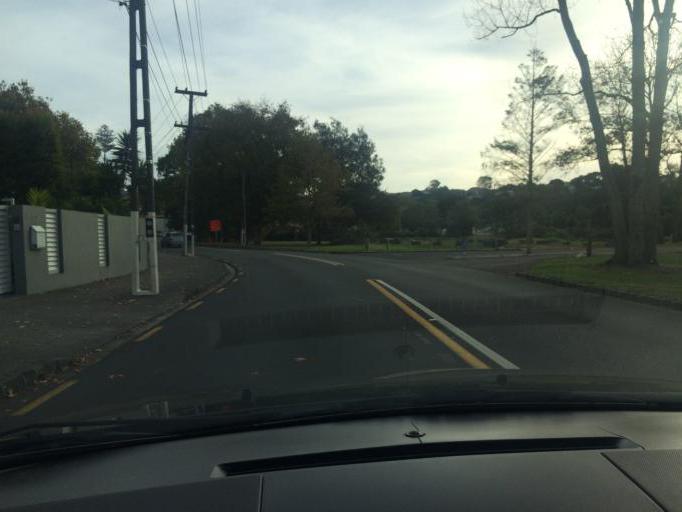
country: NZ
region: Auckland
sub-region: Auckland
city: Auckland
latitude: -36.8652
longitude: 174.7915
